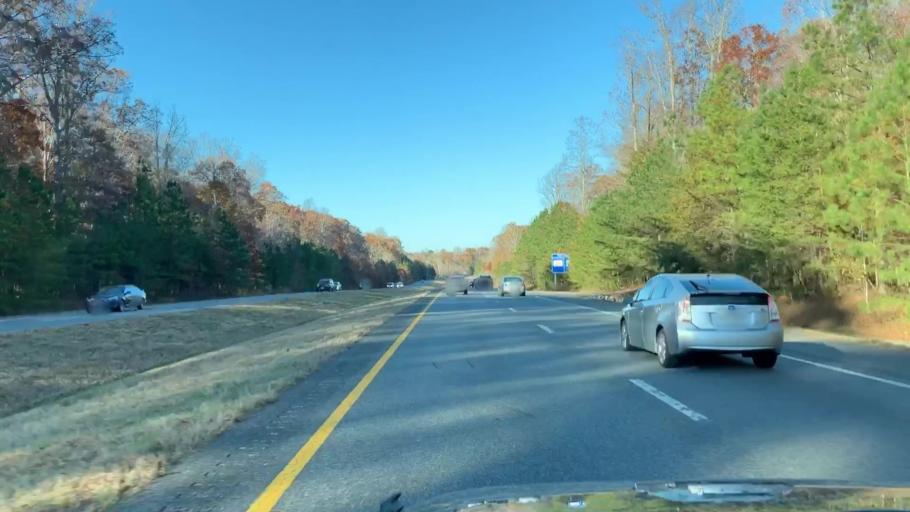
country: US
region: Virginia
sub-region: James City County
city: Williamsburg
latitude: 37.2844
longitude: -76.7532
